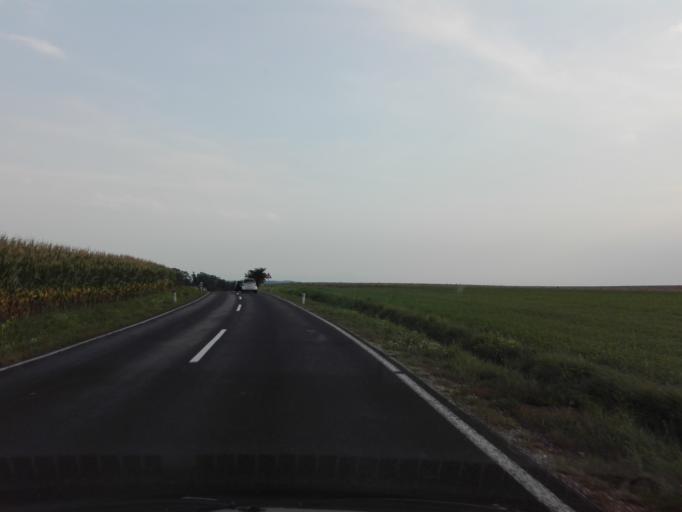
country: AT
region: Upper Austria
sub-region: Politischer Bezirk Grieskirchen
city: Grieskirchen
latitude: 48.2620
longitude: 13.8134
